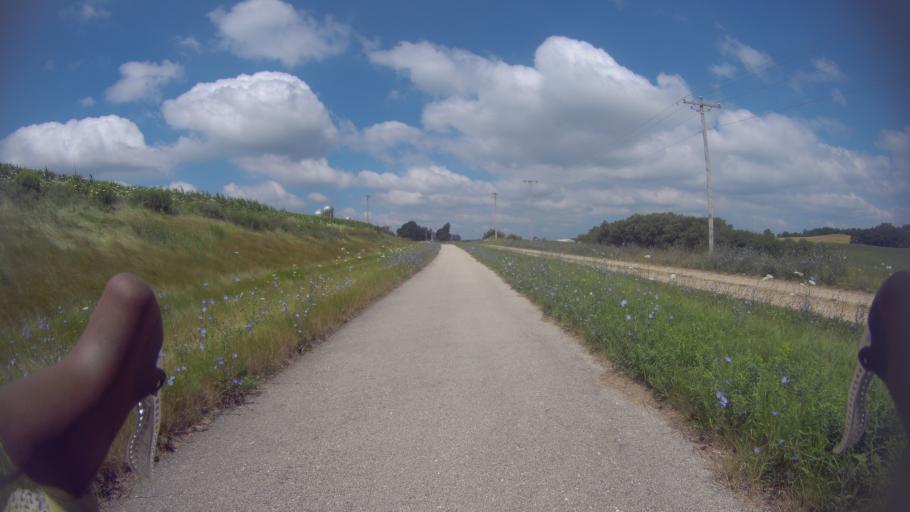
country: US
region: Wisconsin
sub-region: Dane County
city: Waunakee
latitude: 43.1788
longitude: -89.5439
